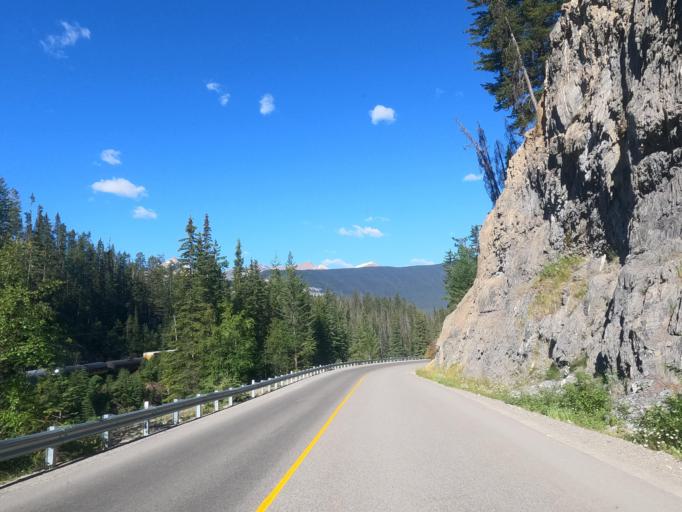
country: CA
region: Alberta
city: Lake Louise
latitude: 51.3807
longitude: -116.5221
